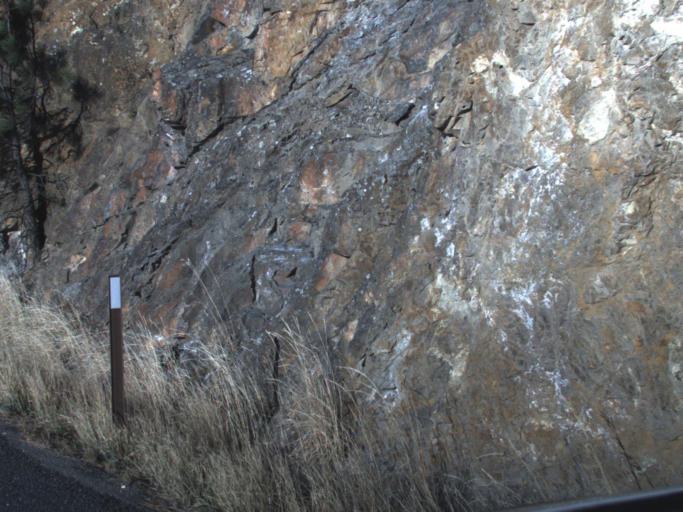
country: US
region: Washington
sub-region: Stevens County
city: Kettle Falls
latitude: 48.6386
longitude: -118.0825
